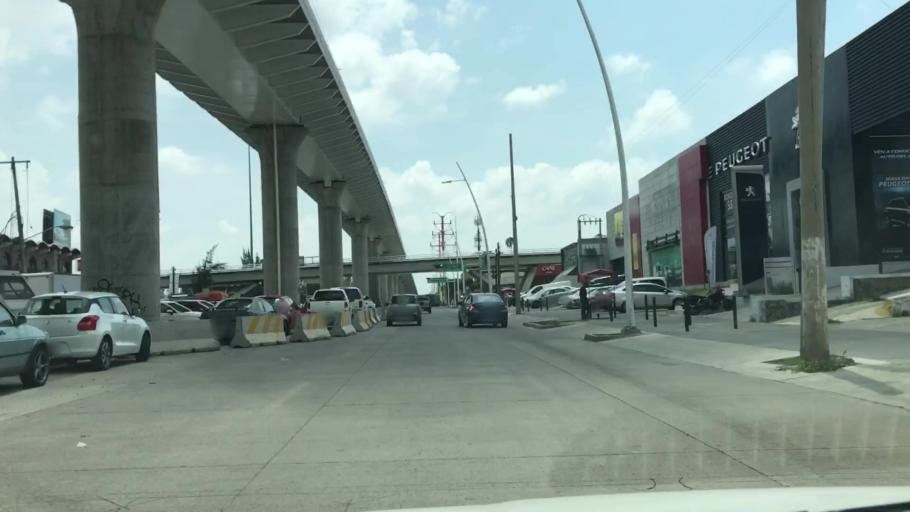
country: MX
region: Jalisco
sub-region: Zapopan
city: Zapopan
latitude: 20.7063
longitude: -103.3658
